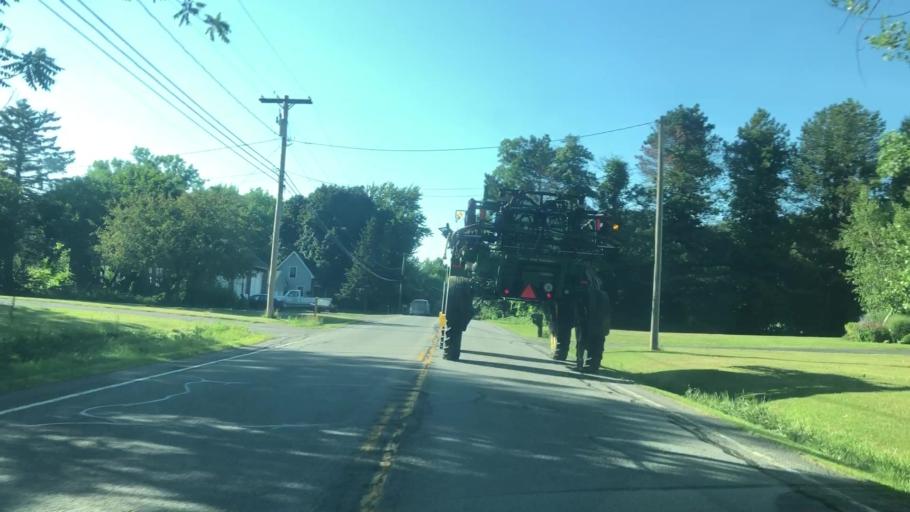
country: US
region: New York
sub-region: Wayne County
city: Ontario
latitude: 43.1954
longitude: -77.2948
